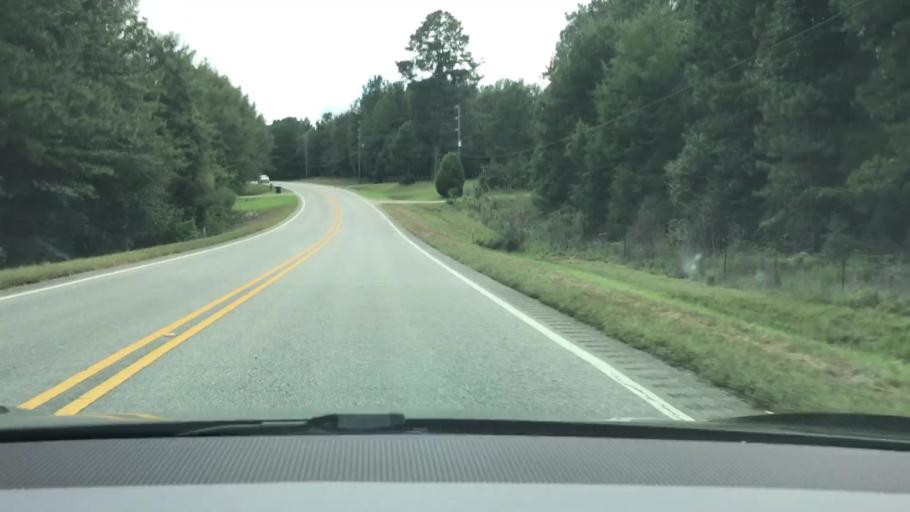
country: US
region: Alabama
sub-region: Pike County
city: Troy
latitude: 31.6533
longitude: -85.9673
